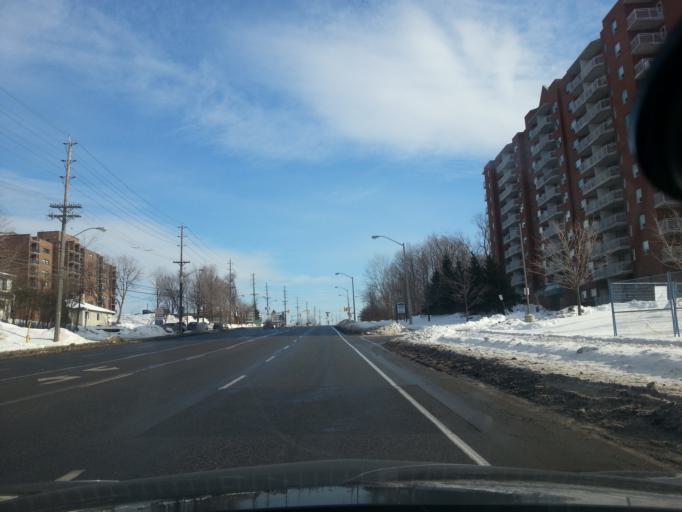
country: CA
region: Ontario
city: Ottawa
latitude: 45.4454
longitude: -75.6336
